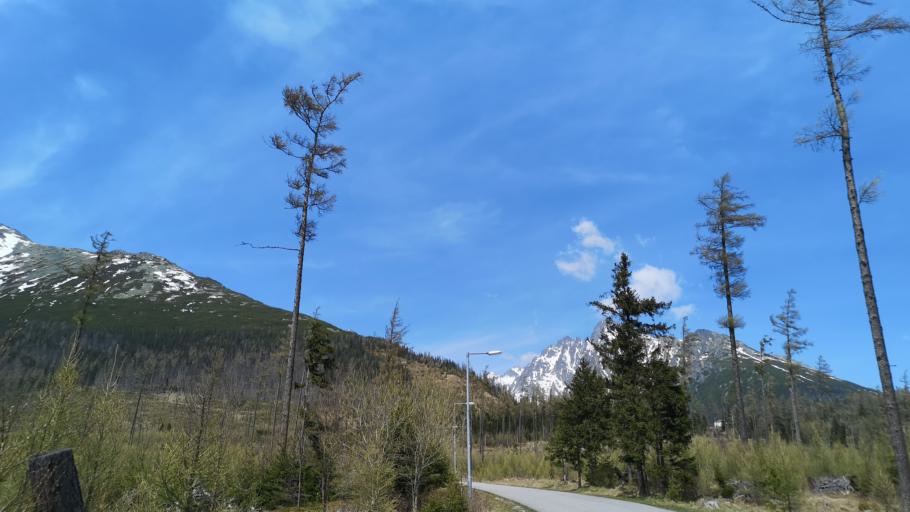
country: SK
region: Presovsky
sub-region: Okres Poprad
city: Vysoke Tatry
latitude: 49.1531
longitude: 20.2262
